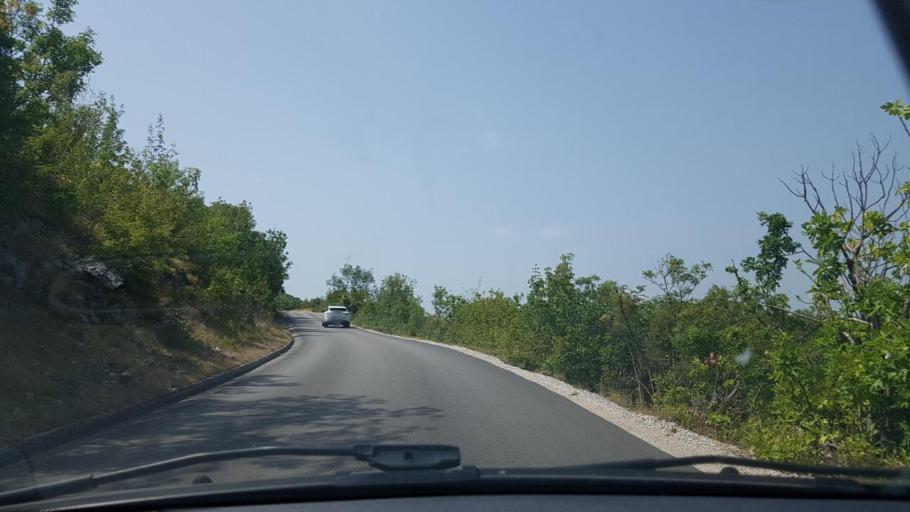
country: HR
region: Dubrovacko-Neretvanska
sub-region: Grad Dubrovnik
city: Metkovic
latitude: 43.0383
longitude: 17.7161
